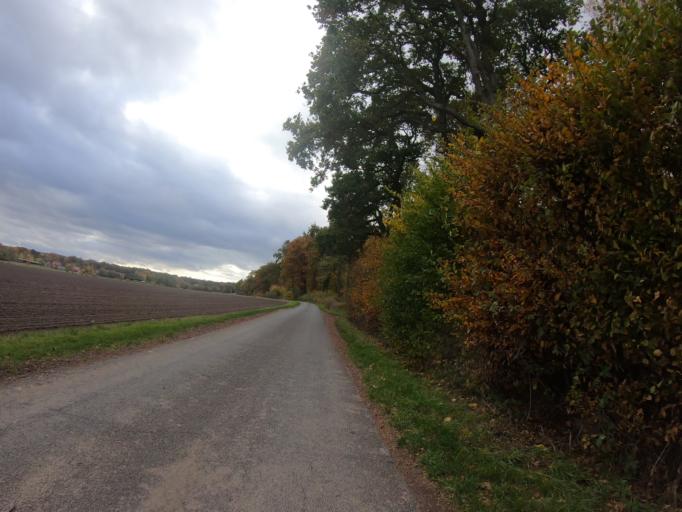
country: DE
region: Lower Saxony
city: Adenbuettel
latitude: 52.4079
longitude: 10.4757
